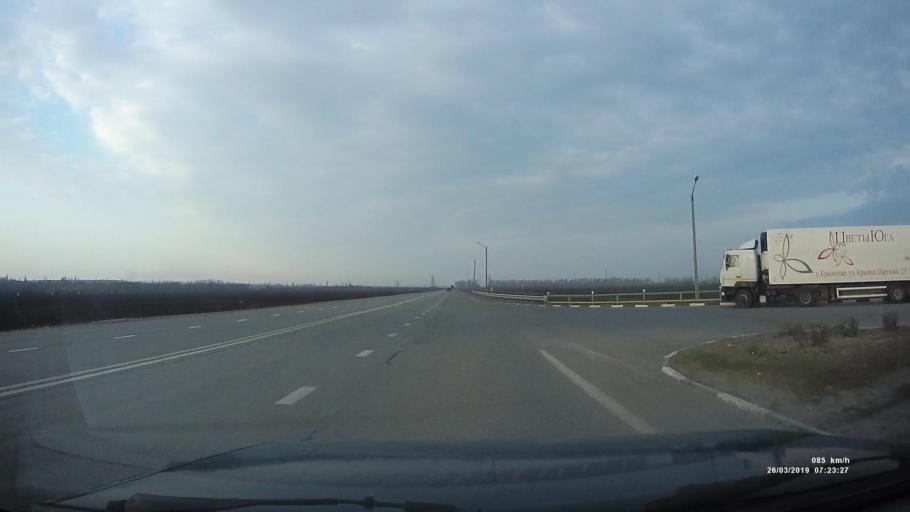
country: RU
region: Rostov
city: Taganrog
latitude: 47.2851
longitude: 38.8758
